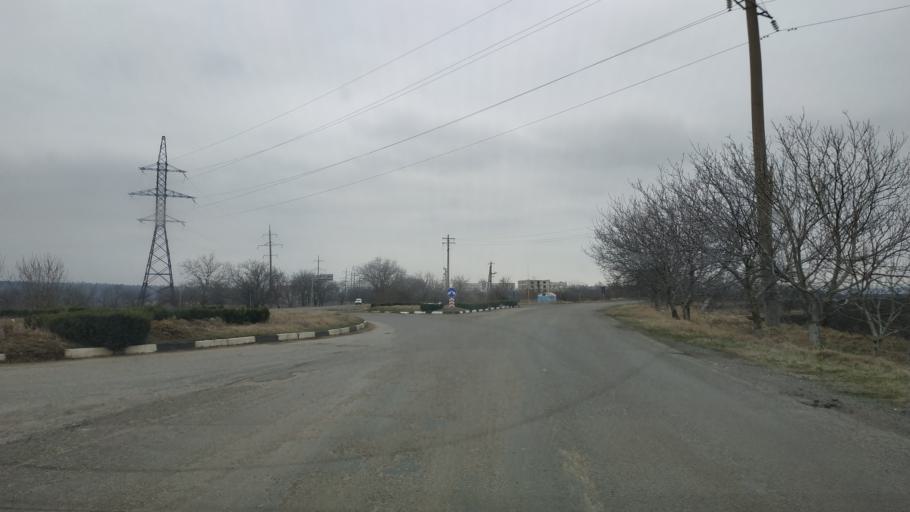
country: MD
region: Cantemir
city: Cantemir
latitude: 46.2840
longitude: 28.2107
